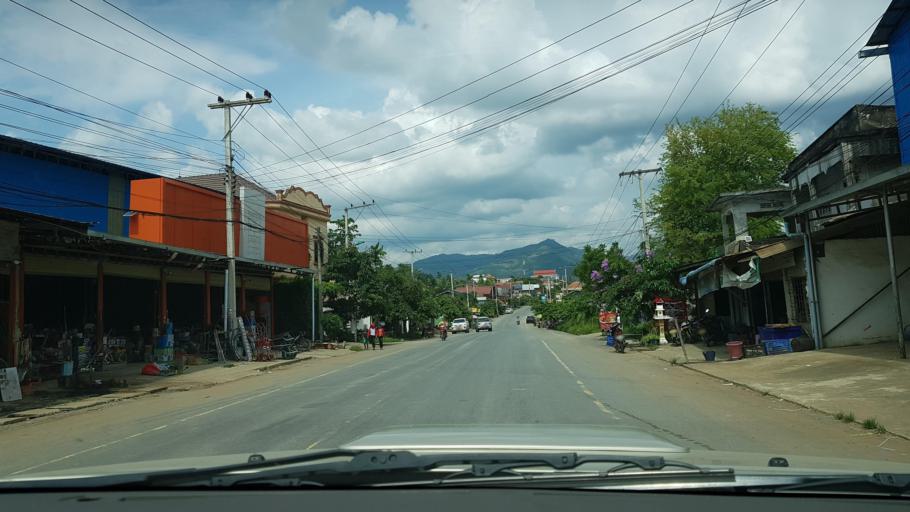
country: LA
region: Loungnamtha
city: Muang Nale
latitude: 20.1471
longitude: 101.4595
